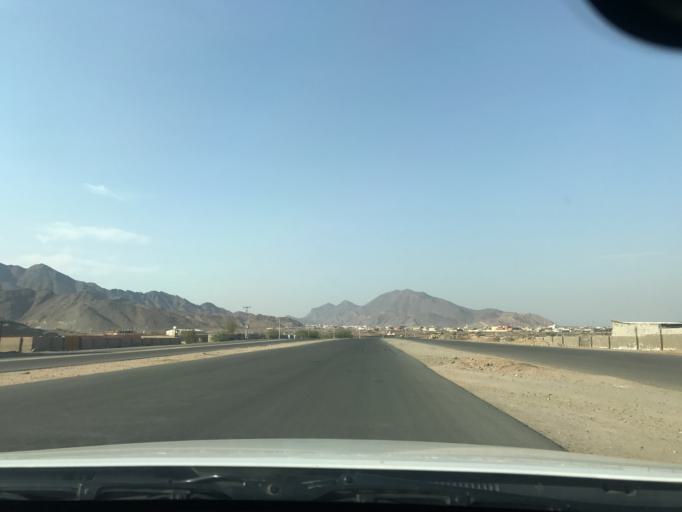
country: SA
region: Makkah
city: Al Jumum
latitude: 21.4476
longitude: 39.5203
